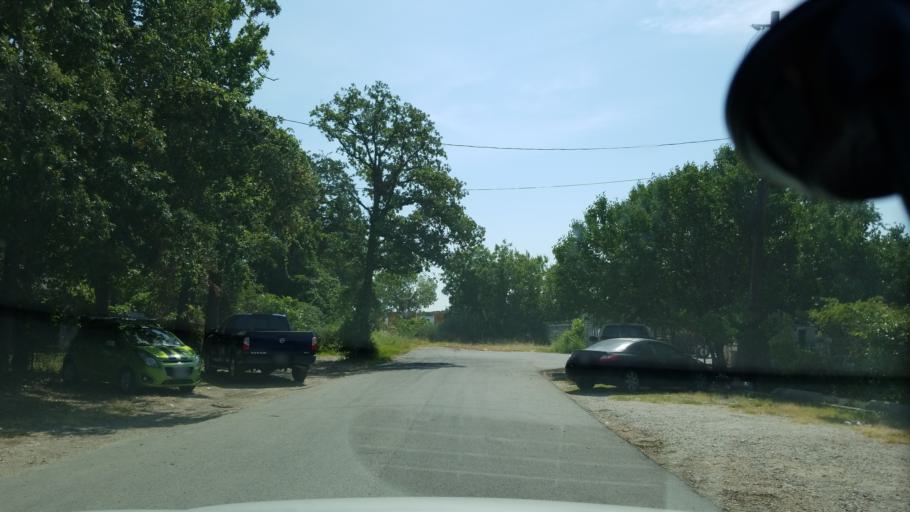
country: US
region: Texas
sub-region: Dallas County
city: Farmers Branch
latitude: 32.8993
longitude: -96.9064
